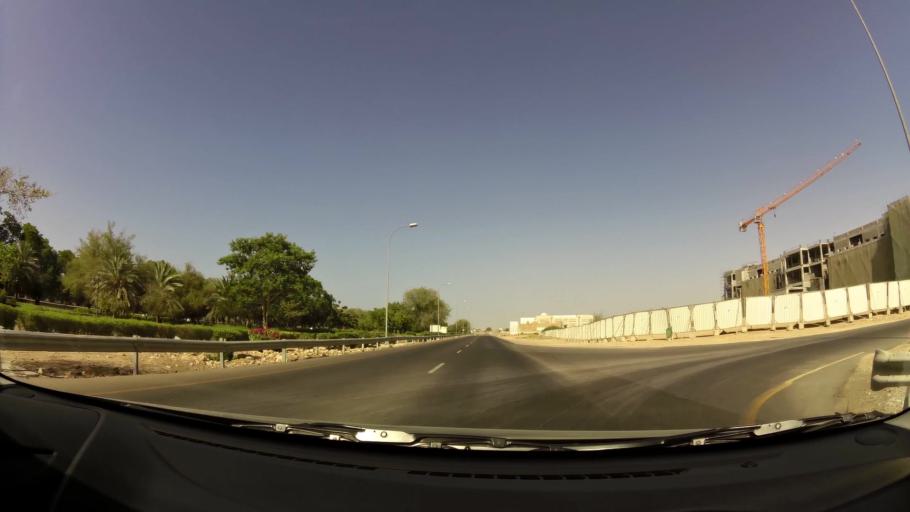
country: OM
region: Muhafazat Masqat
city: Bawshar
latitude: 23.5882
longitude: 58.3146
